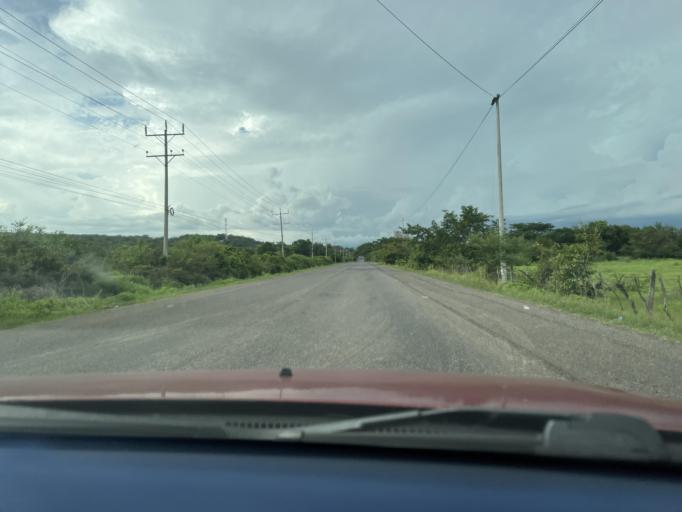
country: SV
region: La Union
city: San Alejo
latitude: 13.3895
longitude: -87.9028
